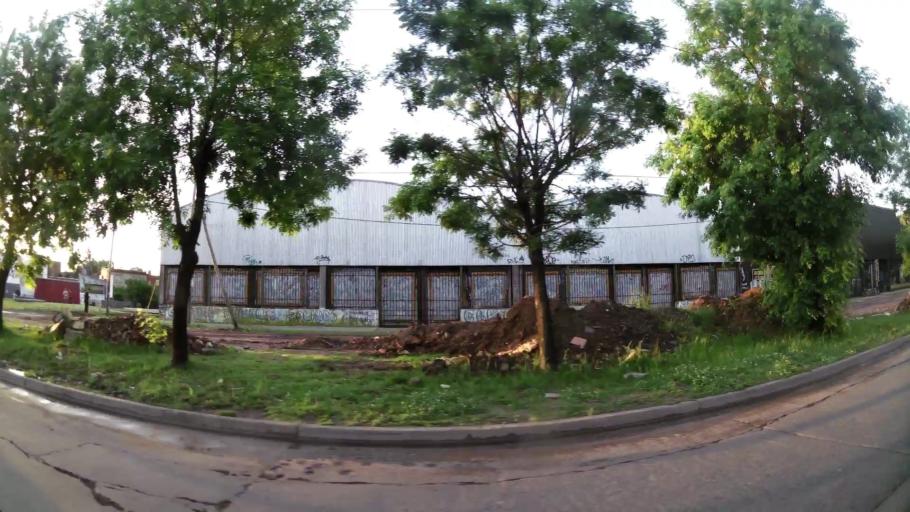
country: AR
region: Buenos Aires
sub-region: Partido de Lomas de Zamora
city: Lomas de Zamora
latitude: -34.7627
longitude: -58.3642
